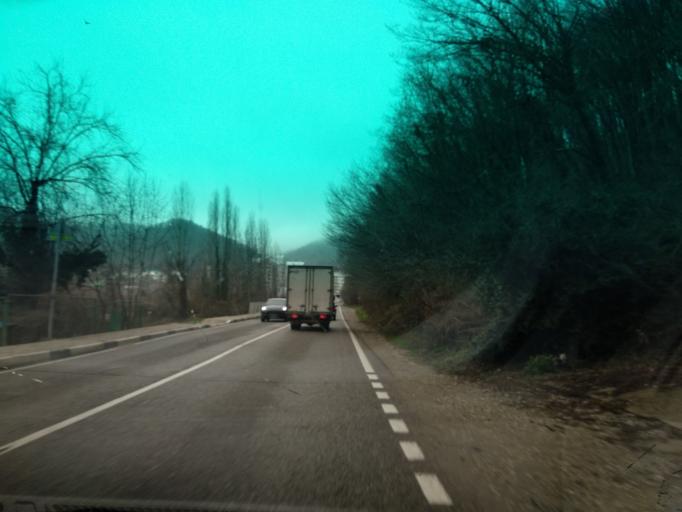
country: RU
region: Krasnodarskiy
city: Agoy
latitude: 44.1432
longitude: 39.0432
